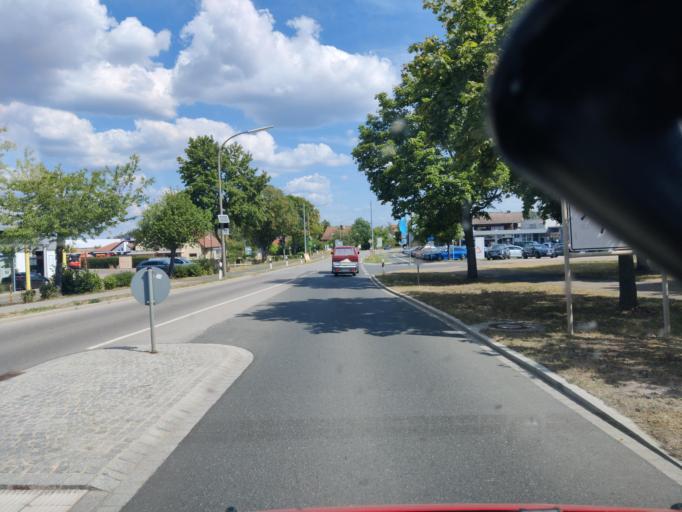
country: DE
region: Bavaria
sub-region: Regierungsbezirk Mittelfranken
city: Hilpoltstein
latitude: 49.1827
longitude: 11.1864
